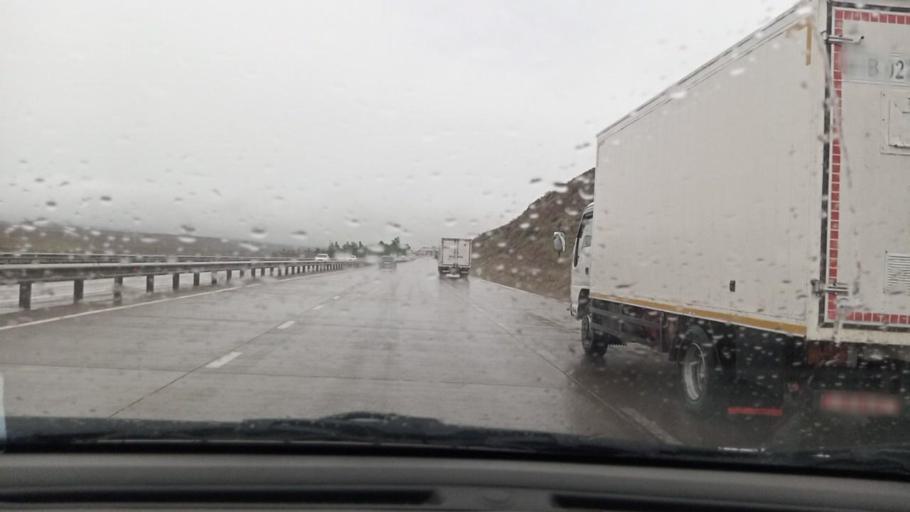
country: UZ
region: Namangan
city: Pop Shahri
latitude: 40.9251
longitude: 70.7253
